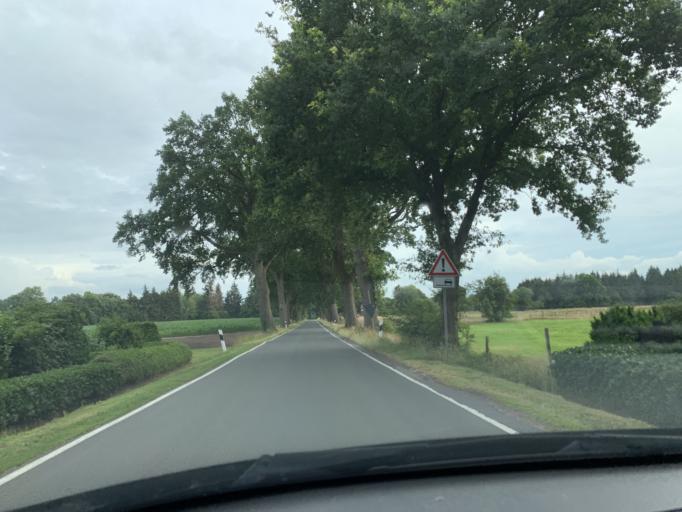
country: DE
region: Lower Saxony
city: Westerstede
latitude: 53.2870
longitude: 7.9216
